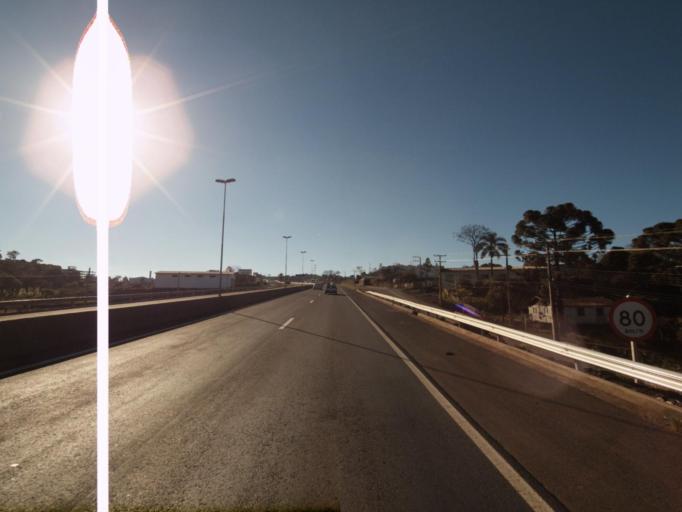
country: BR
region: Santa Catarina
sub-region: Chapeco
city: Chapeco
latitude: -27.0053
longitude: -52.6432
